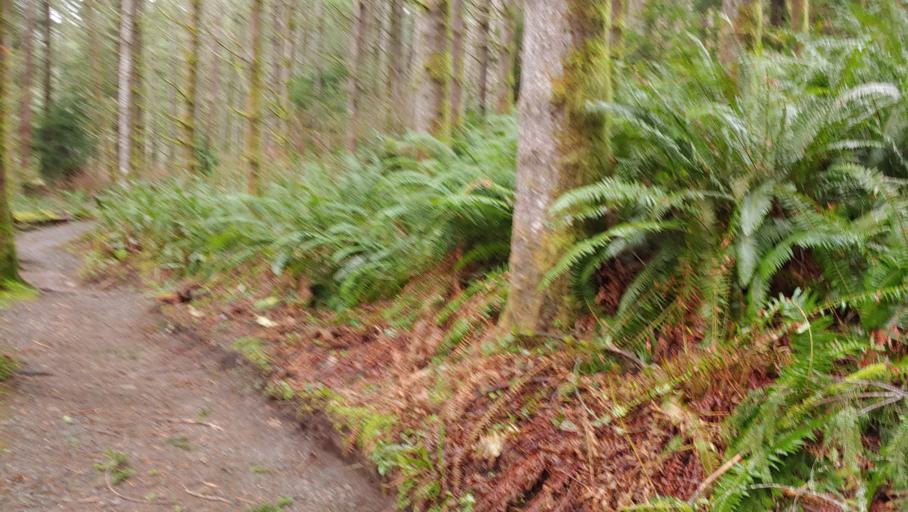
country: US
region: Washington
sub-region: King County
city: Hobart
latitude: 47.4688
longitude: -121.9320
